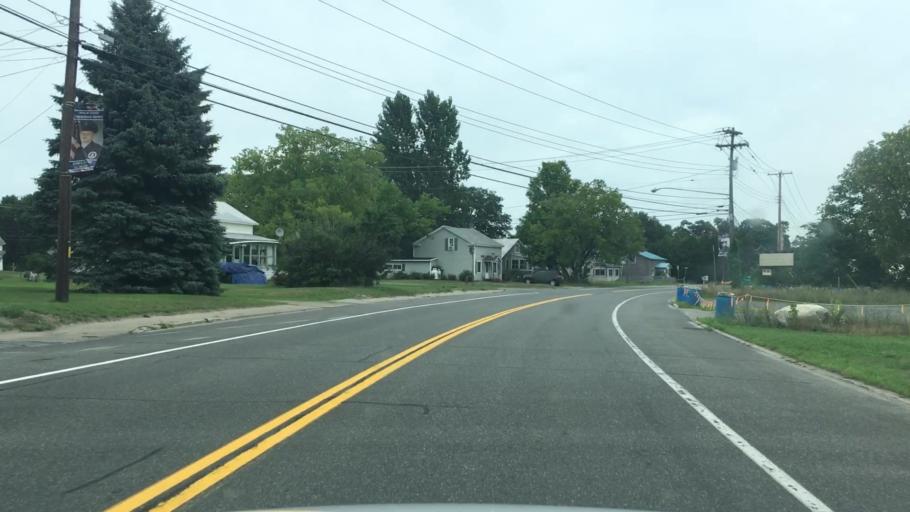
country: US
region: New York
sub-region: Essex County
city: Keeseville
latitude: 44.5011
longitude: -73.4921
